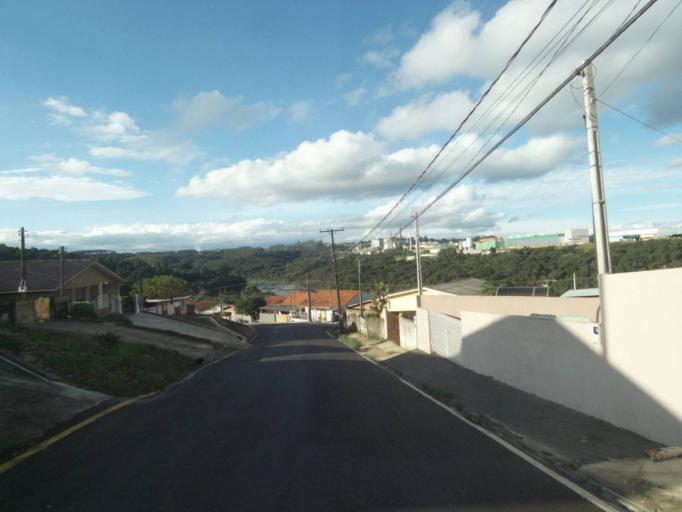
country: BR
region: Parana
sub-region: Telemaco Borba
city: Telemaco Borba
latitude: -24.3246
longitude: -50.6129
